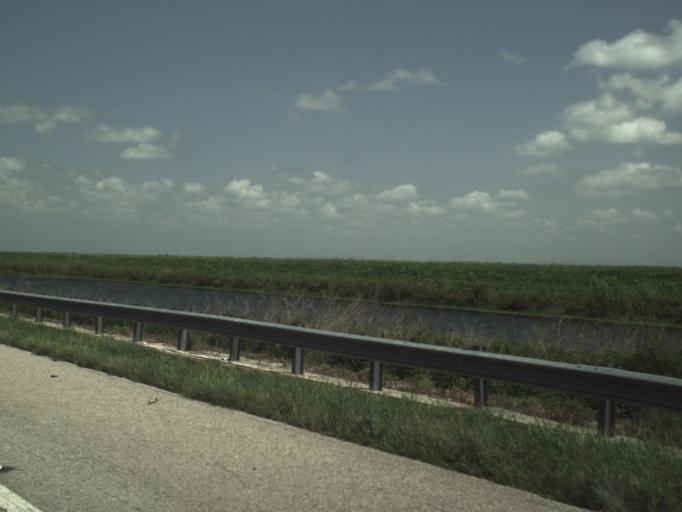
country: US
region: Florida
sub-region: Palm Beach County
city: Belle Glade Camp
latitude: 26.5149
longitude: -80.6771
